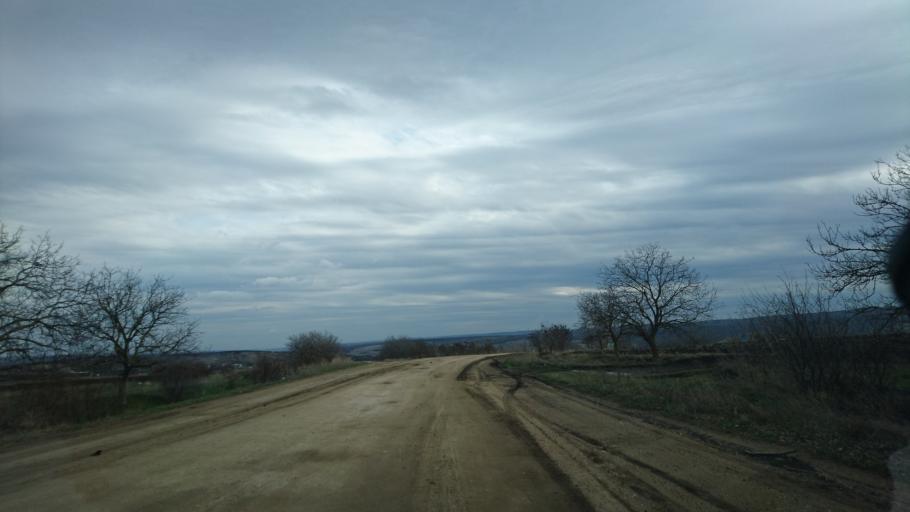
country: MD
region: Cantemir
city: Visniovca
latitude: 46.3390
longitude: 28.4033
